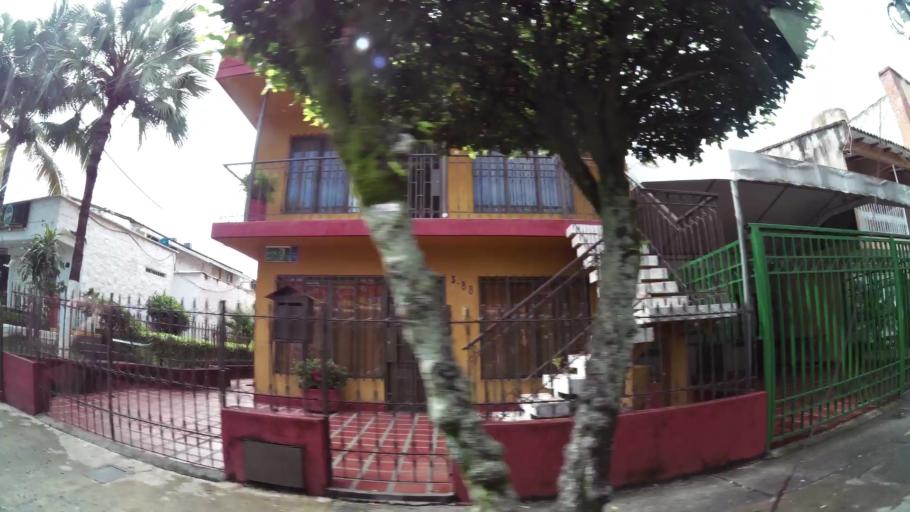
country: CO
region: Valle del Cauca
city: Cali
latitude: 3.3872
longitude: -76.5482
